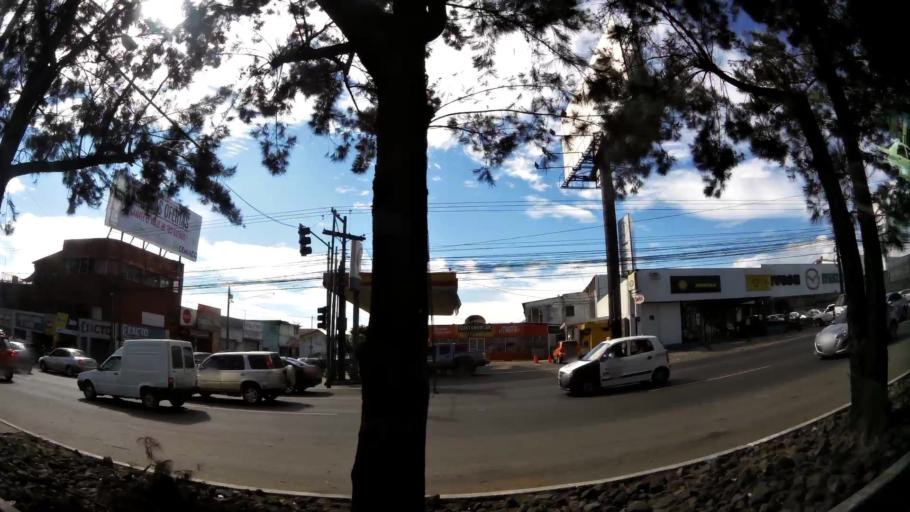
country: GT
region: Guatemala
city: Mixco
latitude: 14.6344
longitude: -90.5837
